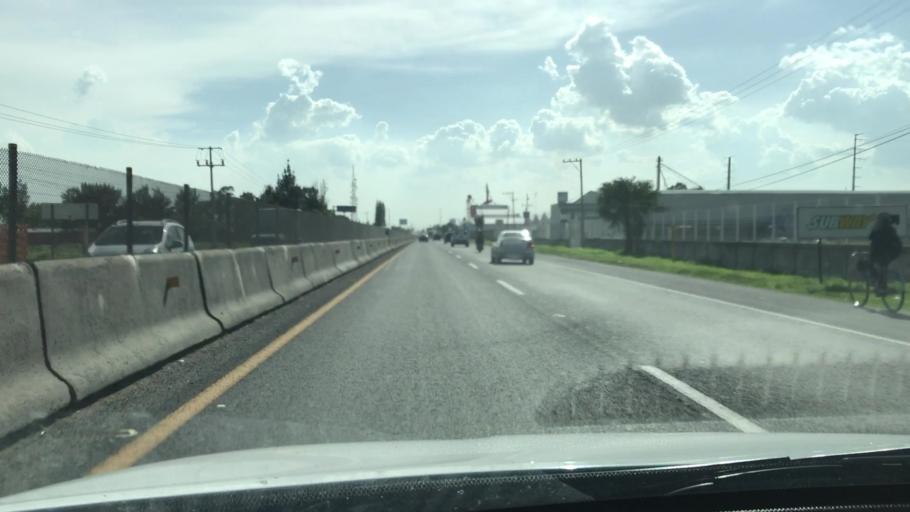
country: MX
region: Guanajuato
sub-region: Cortazar
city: Colonia la Calzada (La Olla)
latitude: 20.5119
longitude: -100.9448
